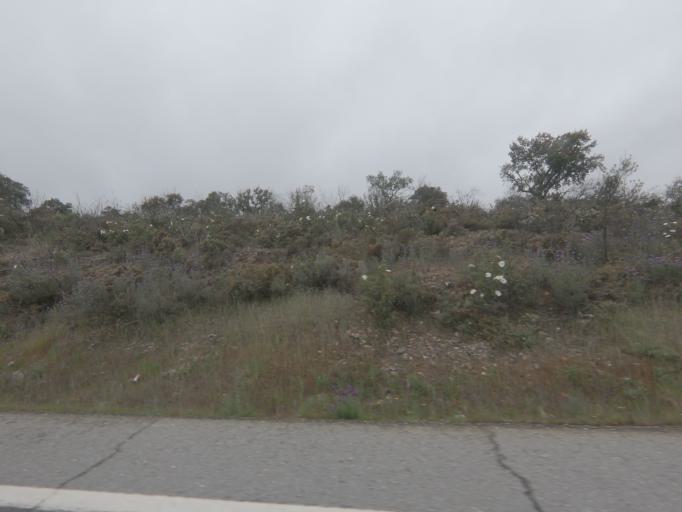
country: ES
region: Extremadura
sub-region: Provincia de Caceres
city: Malpartida de Caceres
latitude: 39.3039
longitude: -6.5158
